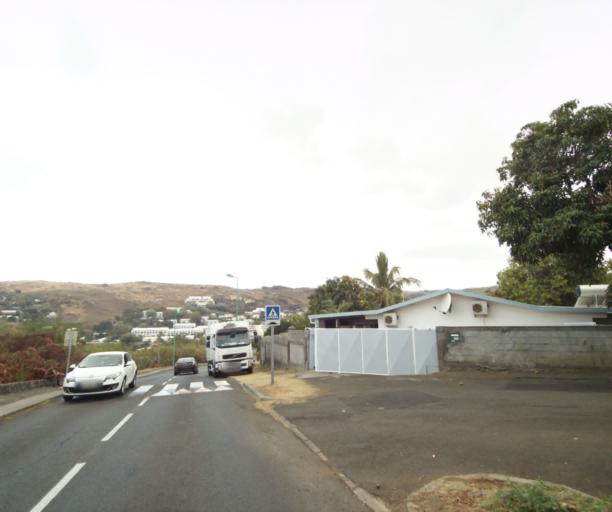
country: RE
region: Reunion
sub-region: Reunion
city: Saint-Paul
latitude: -21.0555
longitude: 55.2283
